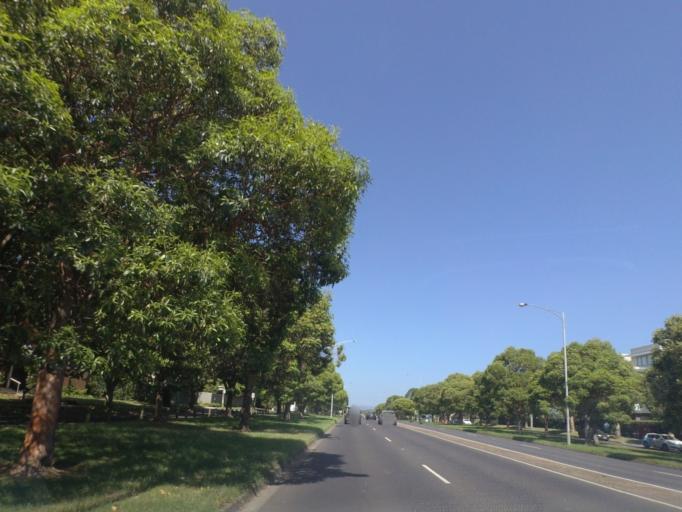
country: AU
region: Victoria
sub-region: Whitehorse
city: Box Hill
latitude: -37.8189
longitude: 145.1314
